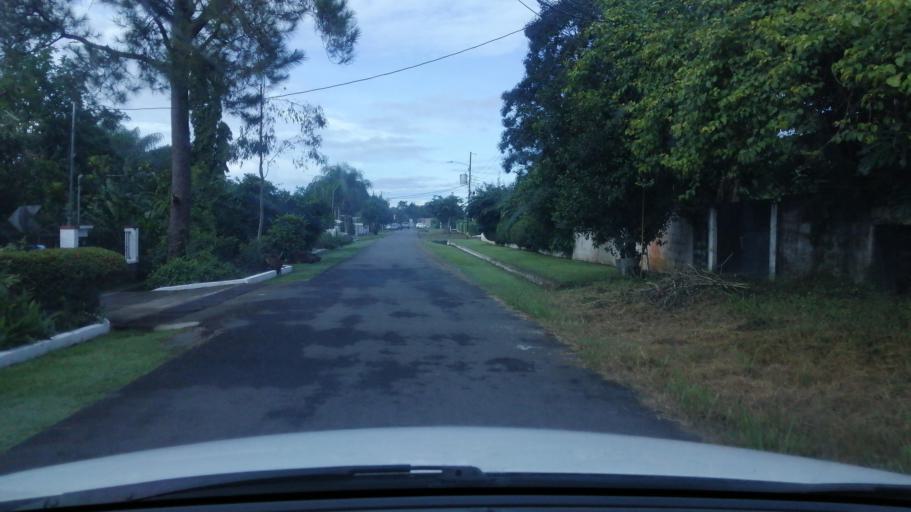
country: PA
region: Chiriqui
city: Mata del Nance
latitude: 8.4551
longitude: -82.4184
